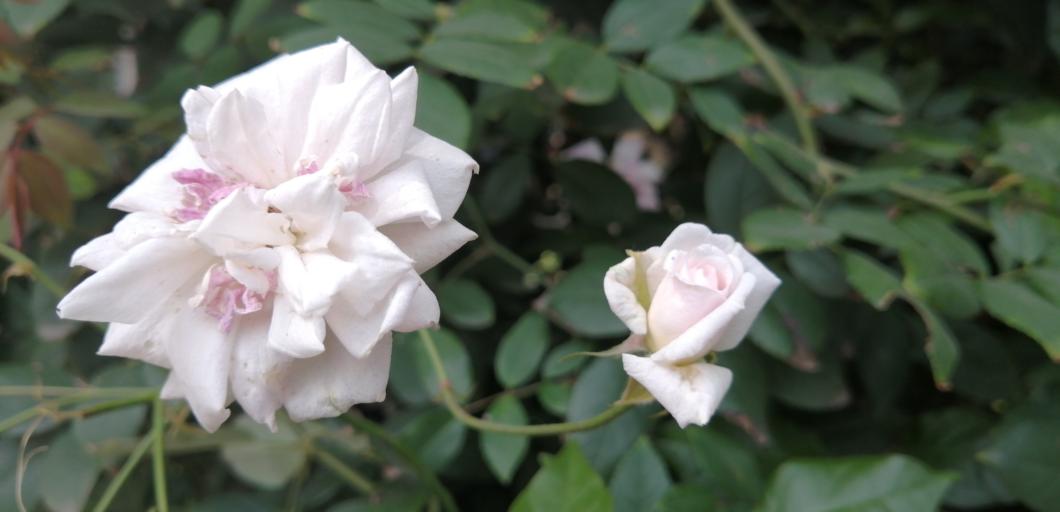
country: MX
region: Mexico City
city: Benito Juarez
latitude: 19.4014
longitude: -99.1477
